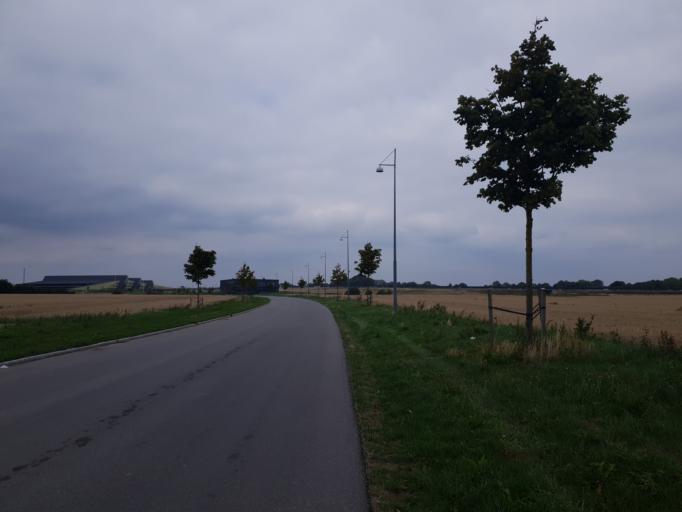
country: DK
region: South Denmark
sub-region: Middelfart Kommune
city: Strib
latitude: 55.4961
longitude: 9.7880
